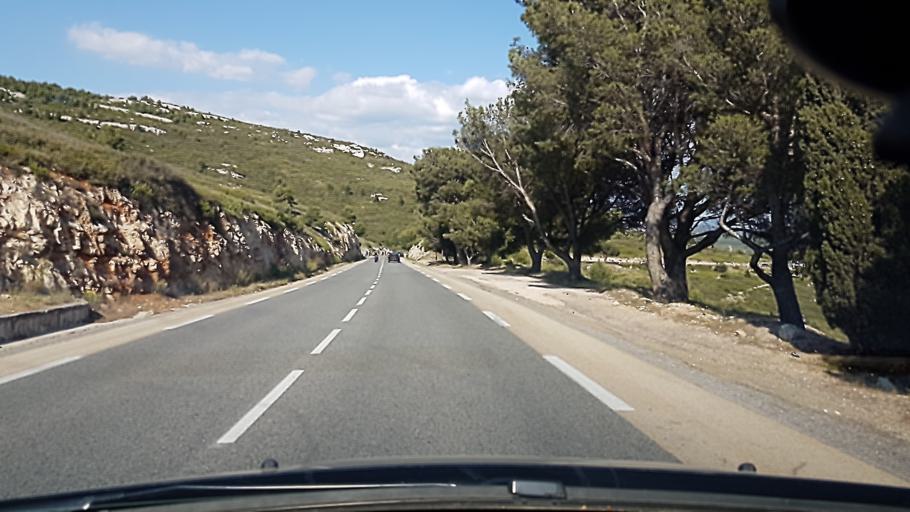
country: FR
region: Provence-Alpes-Cote d'Azur
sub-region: Departement des Bouches-du-Rhone
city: Marseille 11
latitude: 43.2395
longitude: 5.4619
